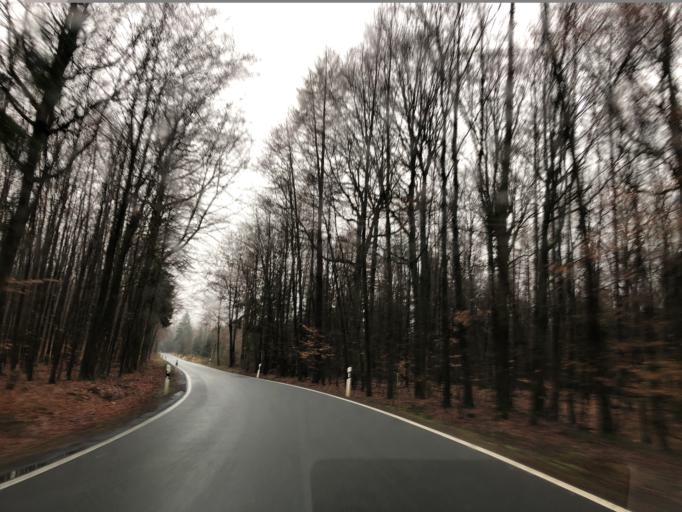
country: DE
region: Hesse
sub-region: Regierungsbezirk Darmstadt
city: Lutzelbach
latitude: 49.7320
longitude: 9.0848
